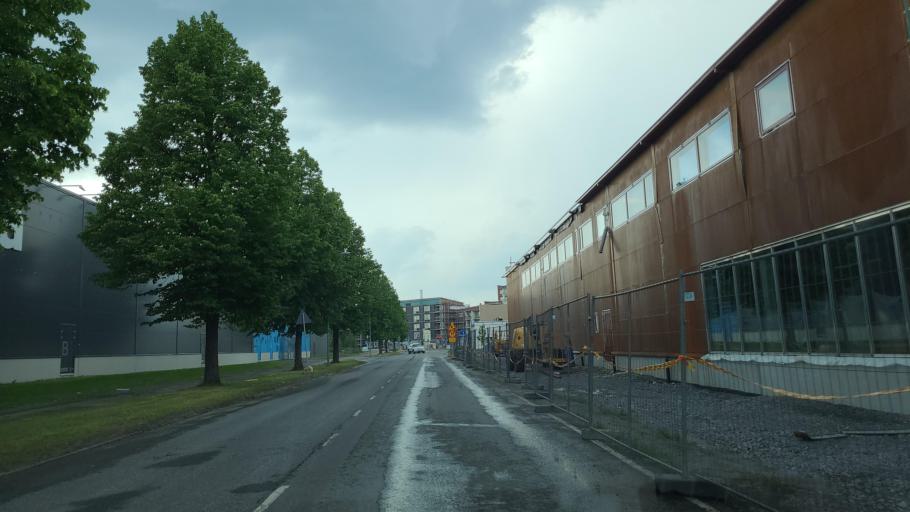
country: FI
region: Ostrobothnia
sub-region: Vaasa
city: Vaasa
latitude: 63.0984
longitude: 21.6362
